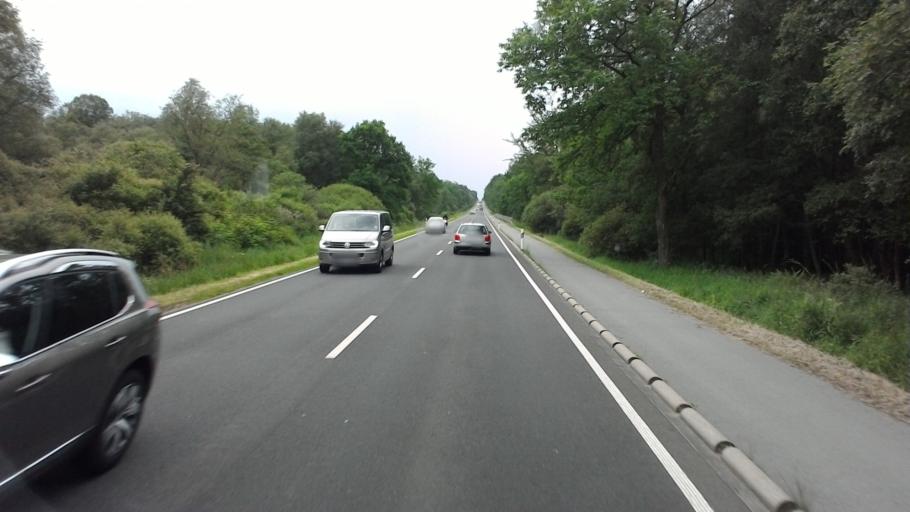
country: DE
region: North Rhine-Westphalia
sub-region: Regierungsbezirk Koln
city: Roetgen
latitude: 50.6234
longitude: 6.2375
